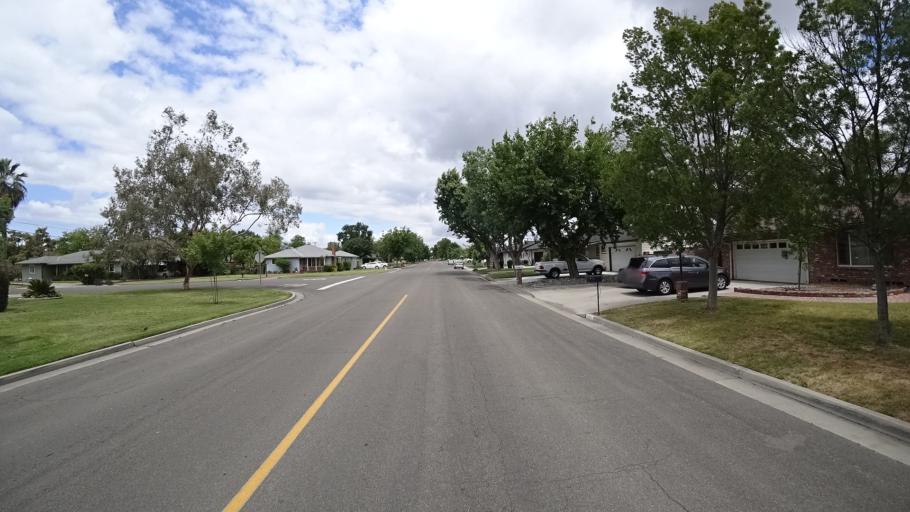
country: US
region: California
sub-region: Kings County
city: Hanford
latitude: 36.3462
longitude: -119.6511
